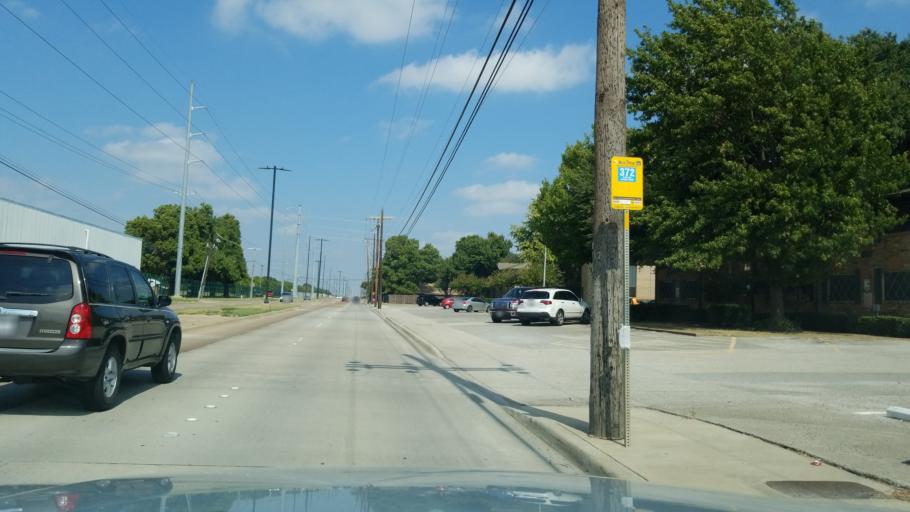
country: US
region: Texas
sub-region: Dallas County
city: Garland
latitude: 32.9021
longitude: -96.6655
